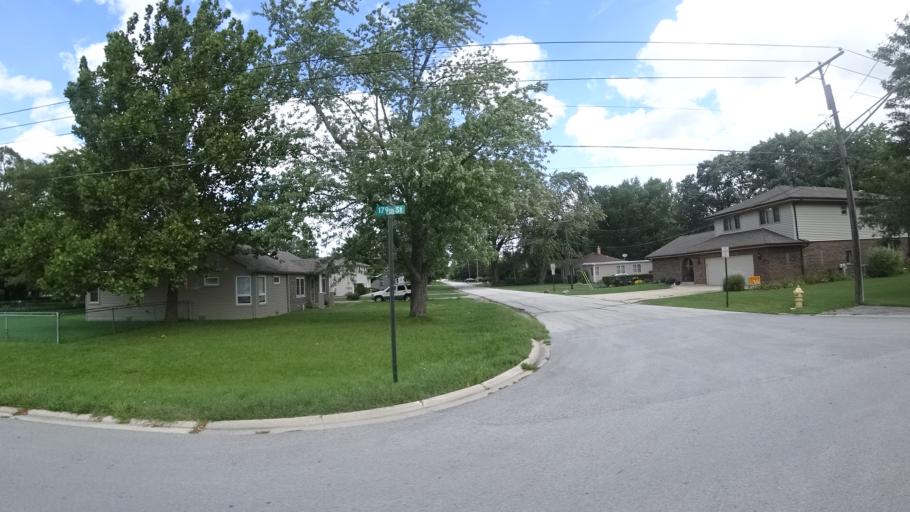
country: US
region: Illinois
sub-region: Cook County
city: Tinley Park
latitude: 41.5660
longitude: -87.7830
